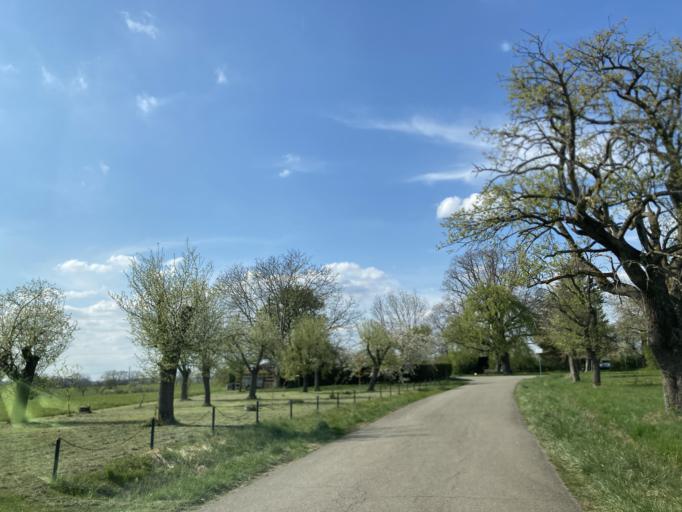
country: DE
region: Baden-Wuerttemberg
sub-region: Tuebingen Region
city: Wannweil
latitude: 48.4799
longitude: 9.1308
